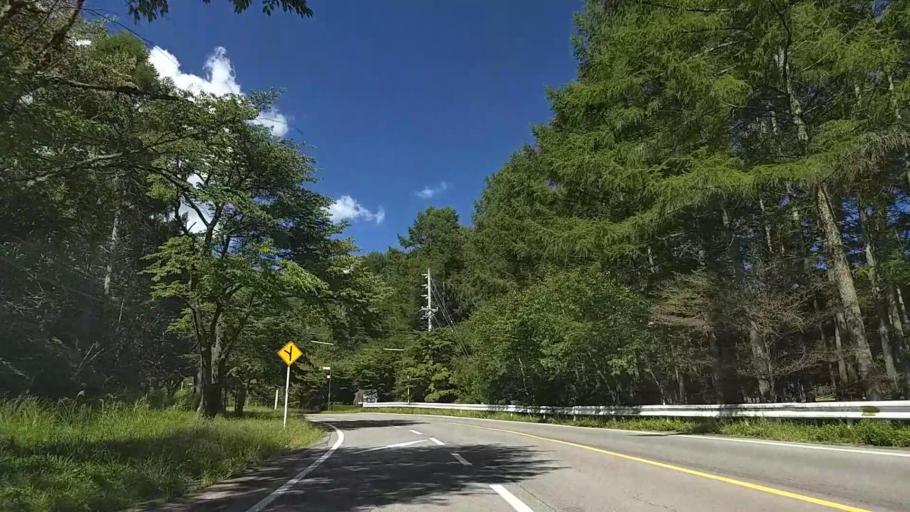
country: JP
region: Nagano
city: Chino
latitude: 36.0415
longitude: 138.2480
